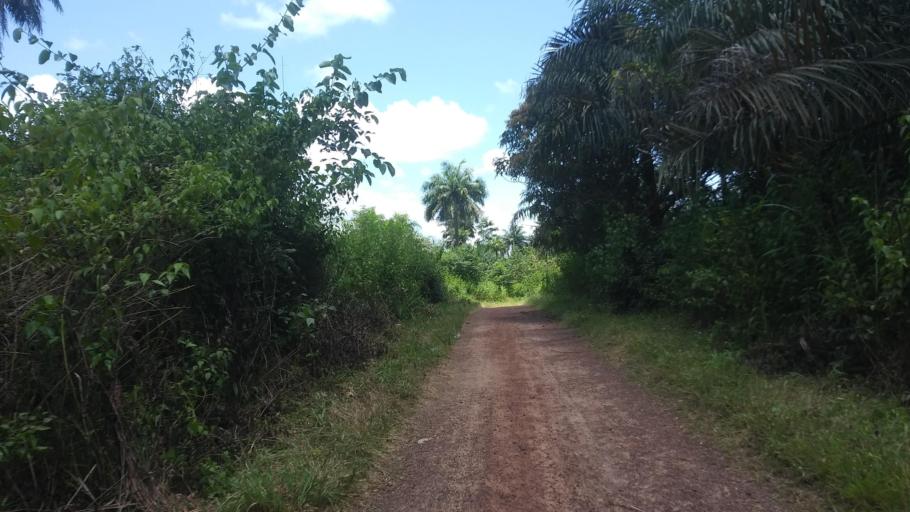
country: SL
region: Northern Province
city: Makeni
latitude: 8.8994
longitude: -11.9948
